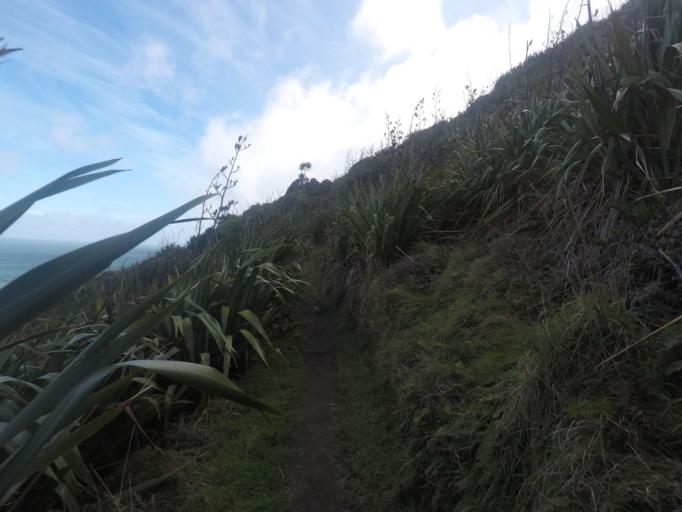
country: NZ
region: Auckland
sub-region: Auckland
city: Muriwai Beach
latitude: -36.8660
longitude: 174.4361
